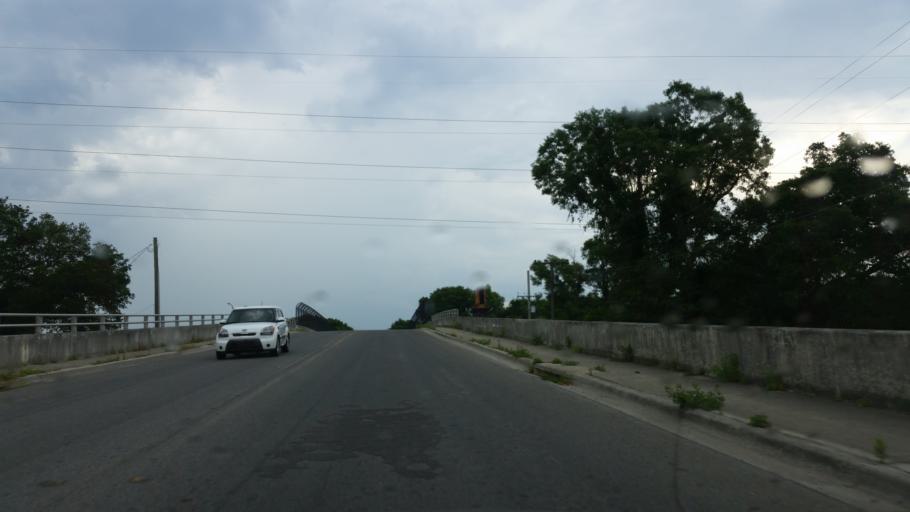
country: US
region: Florida
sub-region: Escambia County
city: Brent
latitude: 30.4613
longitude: -87.2268
